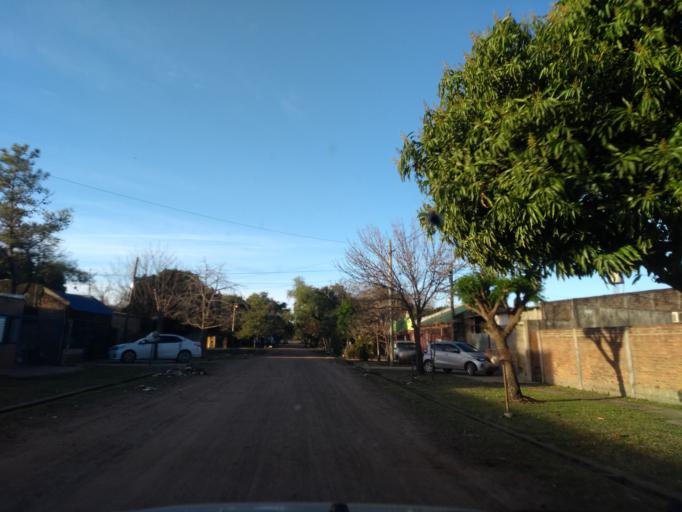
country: AR
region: Chaco
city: Resistencia
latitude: -27.4815
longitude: -58.9649
